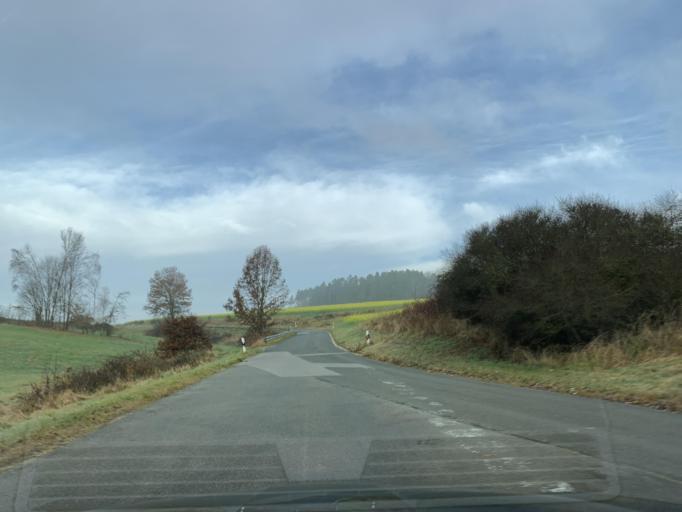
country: DE
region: Bavaria
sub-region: Upper Palatinate
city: Neunburg vorm Wald
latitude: 49.3668
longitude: 12.3937
